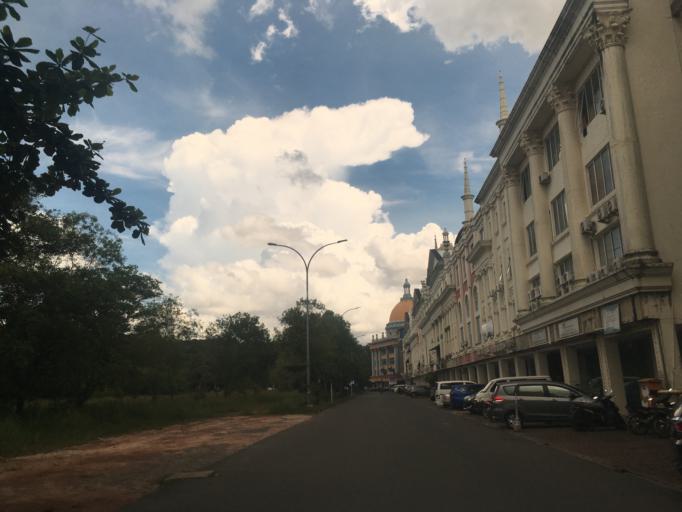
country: SG
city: Singapore
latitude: 1.1176
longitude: 104.0251
